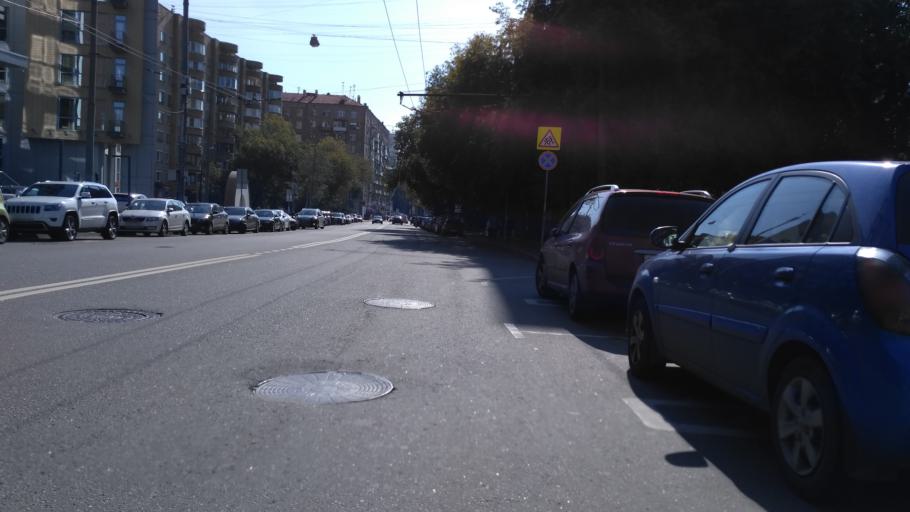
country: RU
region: Moscow
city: Sokol'niki
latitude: 55.7745
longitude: 37.6728
